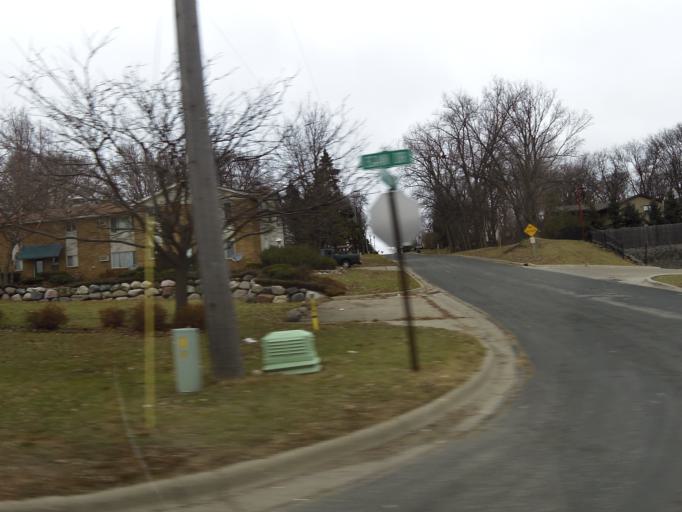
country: US
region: Minnesota
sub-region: Scott County
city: Savage
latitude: 44.7464
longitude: -93.3764
